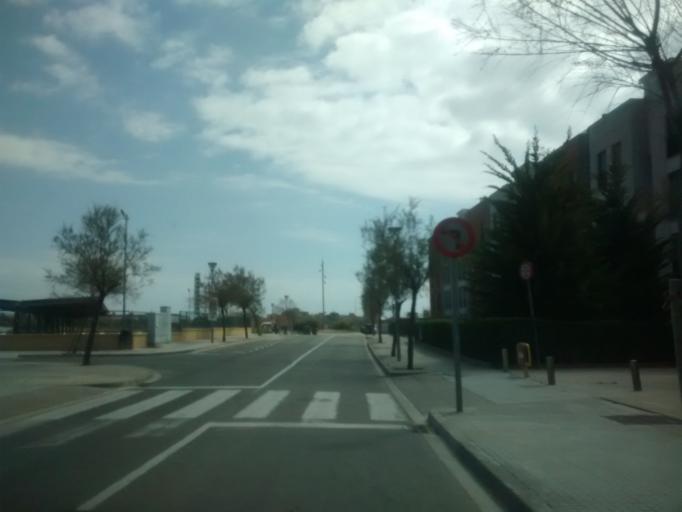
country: ES
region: Catalonia
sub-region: Provincia de Tarragona
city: Cunit
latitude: 41.1980
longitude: 1.6528
